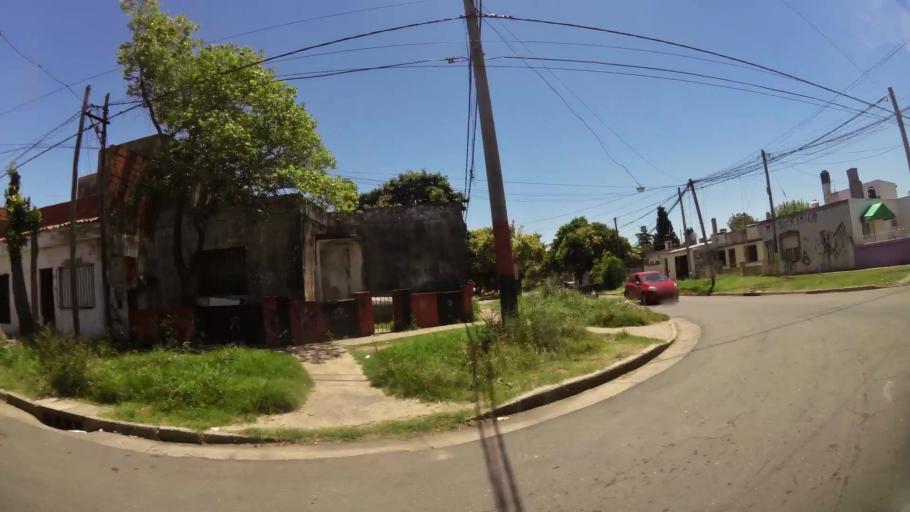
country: AR
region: Santa Fe
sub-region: Departamento de Rosario
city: Rosario
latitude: -32.9544
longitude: -60.7086
